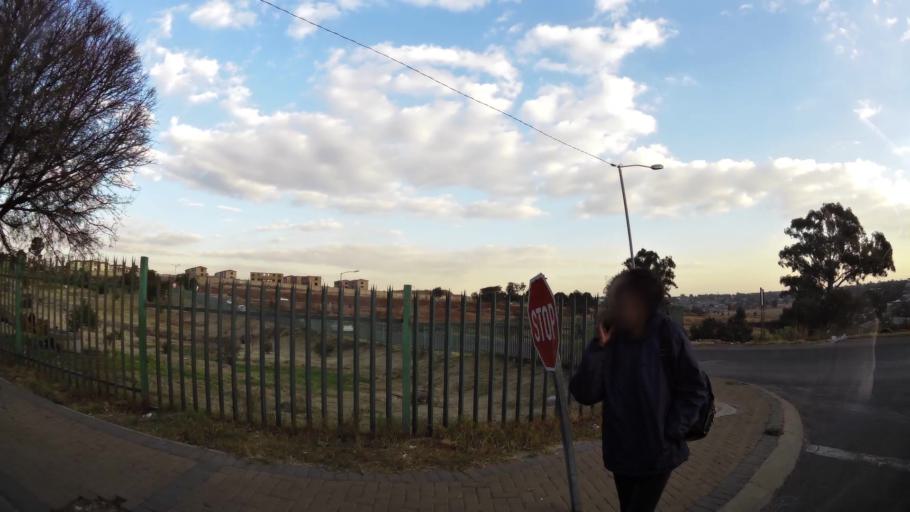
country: ZA
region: Gauteng
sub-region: West Rand District Municipality
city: Krugersdorp
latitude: -26.0823
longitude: 27.7531
